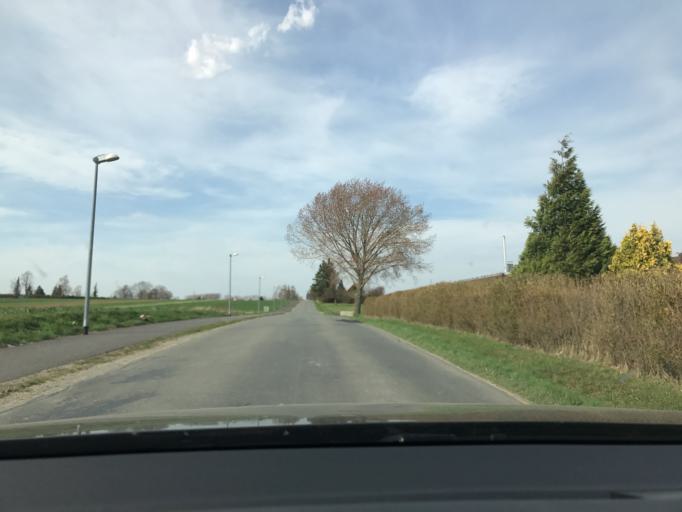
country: DE
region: Thuringia
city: Langula
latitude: 51.1552
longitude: 10.4210
